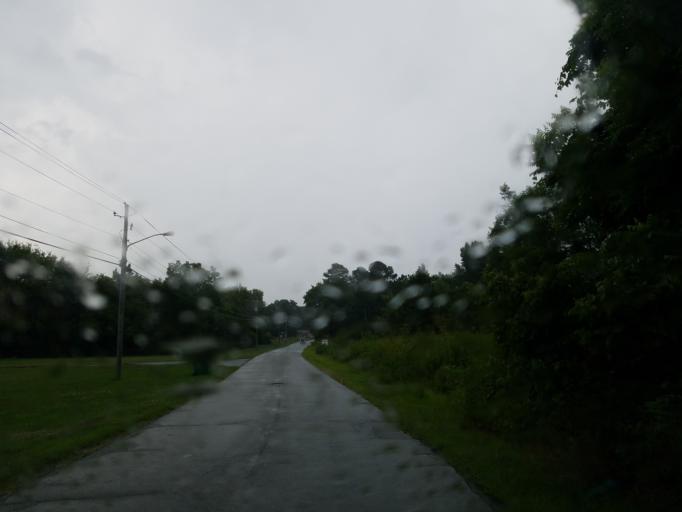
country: US
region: Georgia
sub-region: Bartow County
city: Rydal
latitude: 34.2795
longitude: -84.7525
